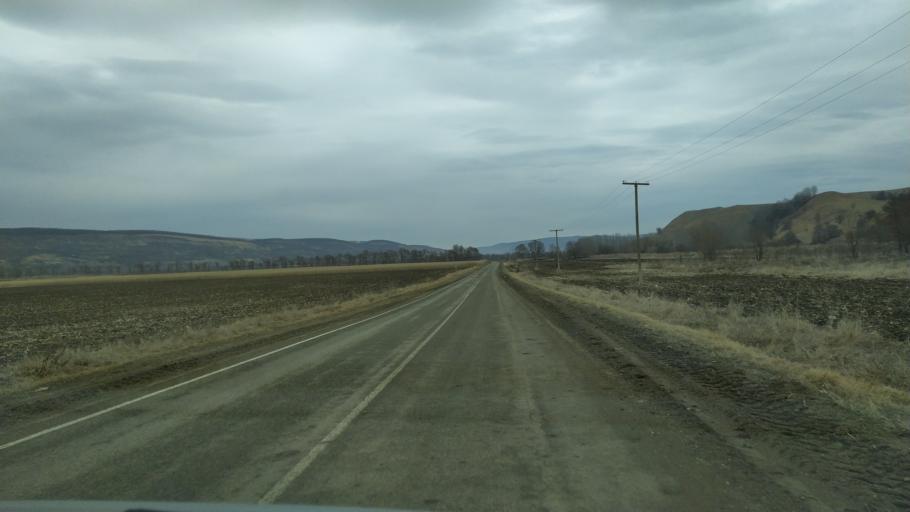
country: RU
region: Krasnodarskiy
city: Peredovaya
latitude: 44.1009
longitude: 41.4094
